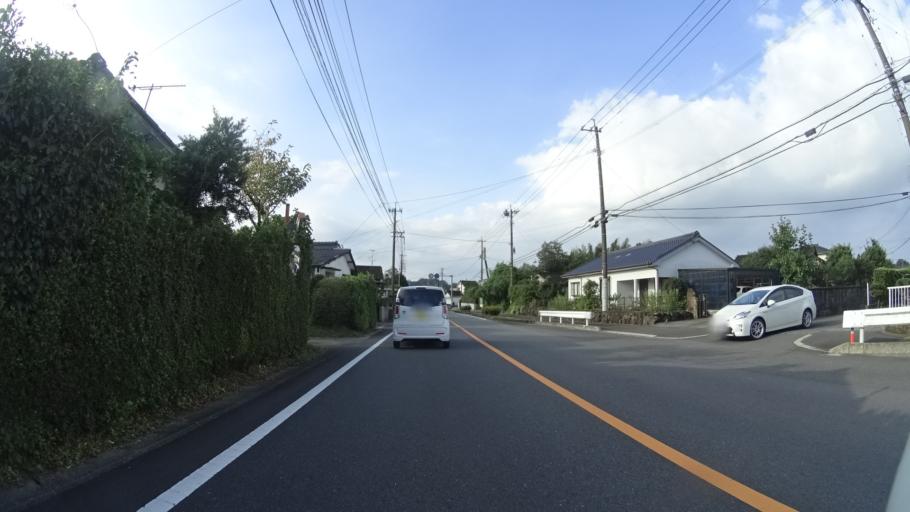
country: JP
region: Kagoshima
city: Okuchi-shinohara
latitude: 32.0305
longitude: 130.5960
